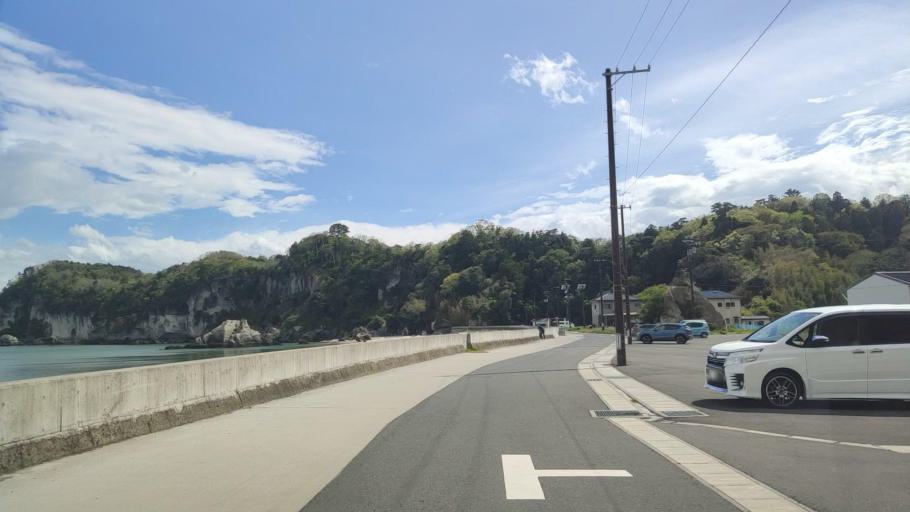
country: JP
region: Miyagi
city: Yamoto
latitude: 38.3355
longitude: 141.1671
